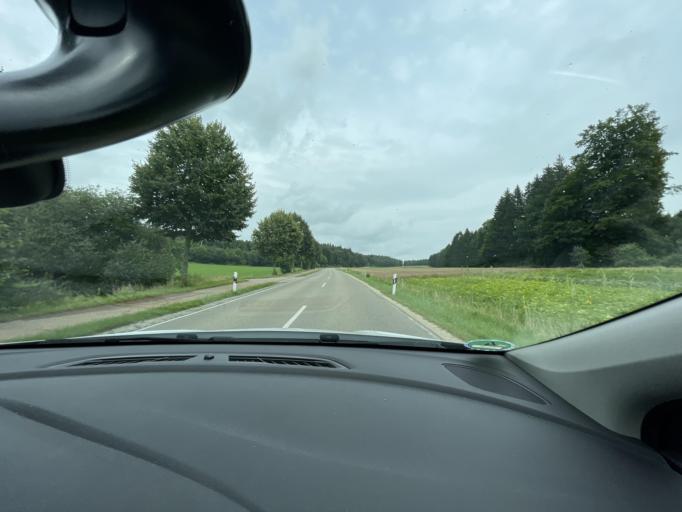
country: DE
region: Bavaria
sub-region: Swabia
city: Thierhaupten
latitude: 48.5634
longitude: 10.9356
